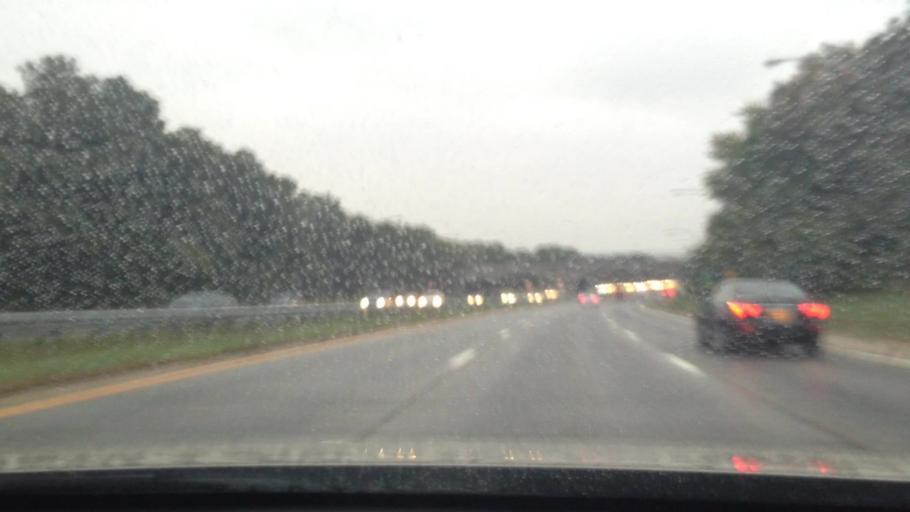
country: US
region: New York
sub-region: Suffolk County
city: North Bay Shore
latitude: 40.7492
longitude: -73.2659
